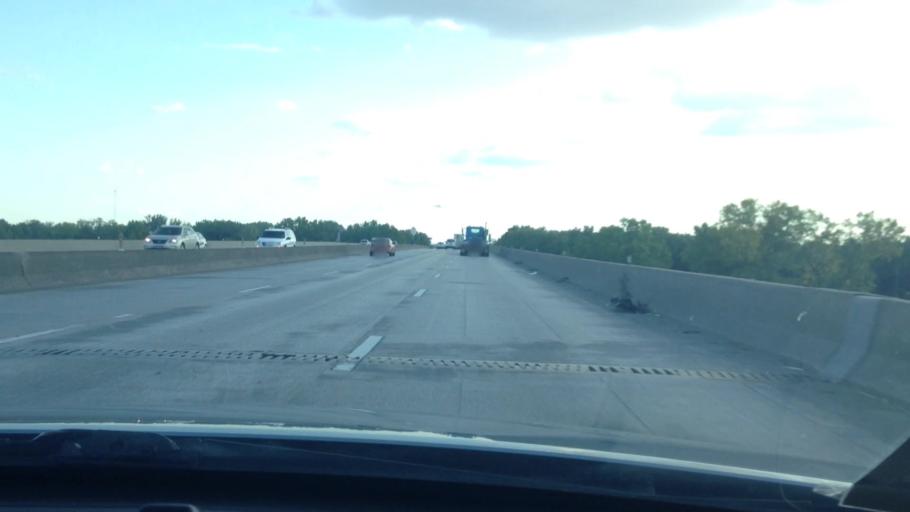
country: US
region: Missouri
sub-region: Clay County
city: Claycomo
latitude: 39.1536
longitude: -94.4982
